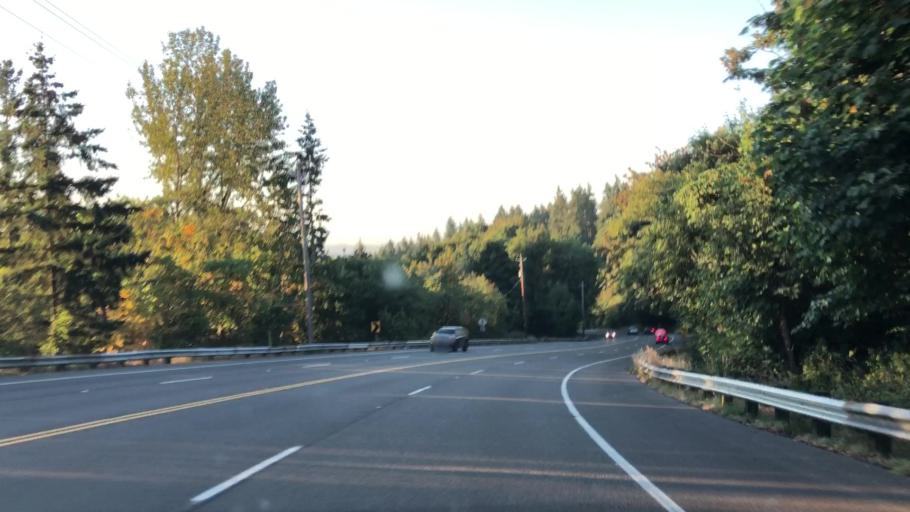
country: US
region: Washington
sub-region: King County
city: Lakeland North
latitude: 47.3570
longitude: -122.2692
